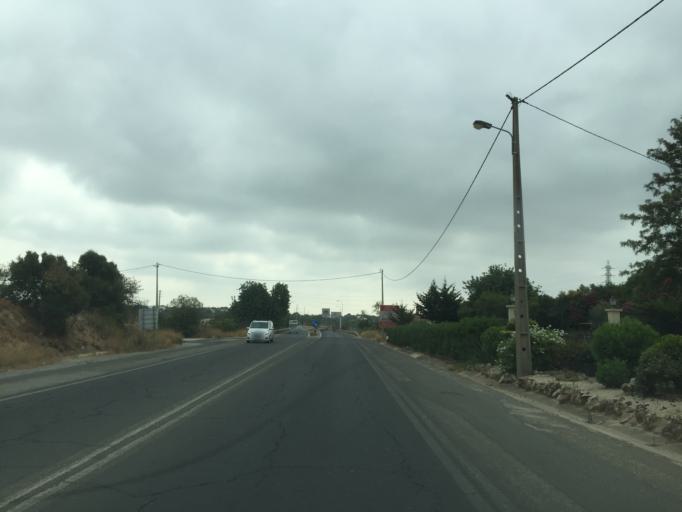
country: PT
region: Faro
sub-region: Faro
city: Santa Barbara de Nexe
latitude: 37.0749
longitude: -7.9823
